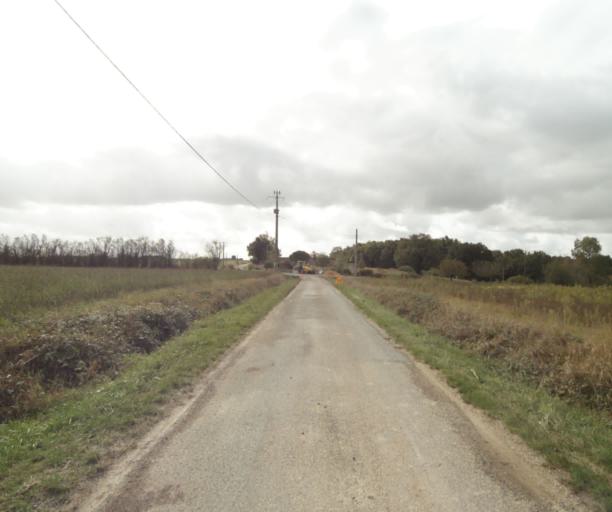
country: FR
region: Midi-Pyrenees
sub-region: Departement du Tarn-et-Garonne
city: Beaumont-de-Lomagne
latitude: 43.8681
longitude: 1.0681
